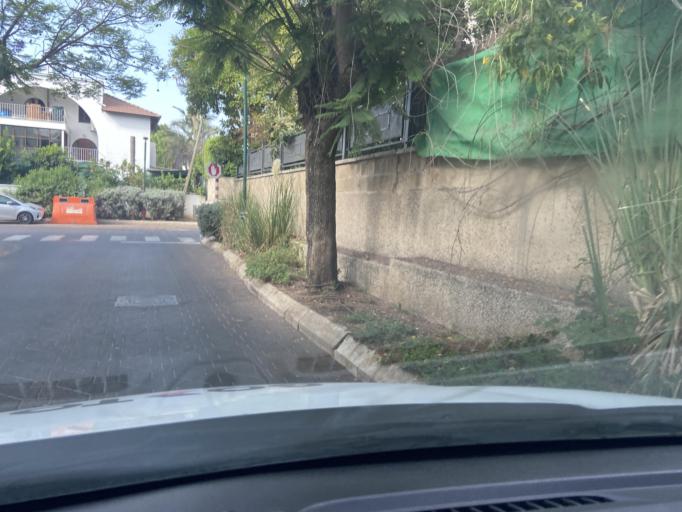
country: IL
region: Central District
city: Yehud
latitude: 32.0349
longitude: 34.8828
